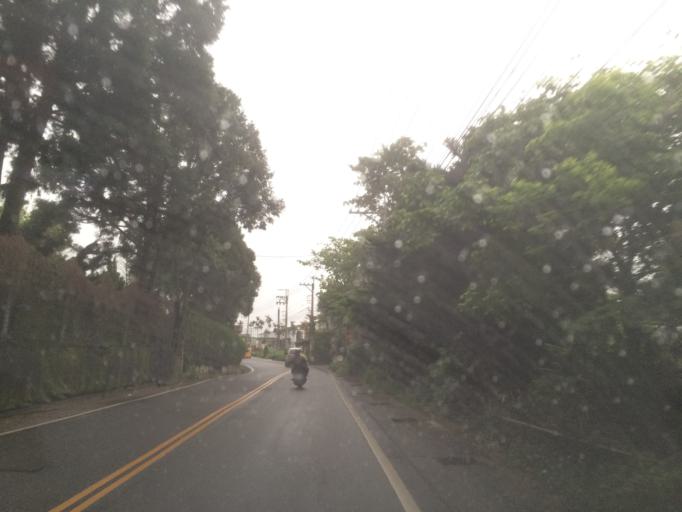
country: TW
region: Taiwan
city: Fengyuan
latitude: 24.1879
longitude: 120.8140
